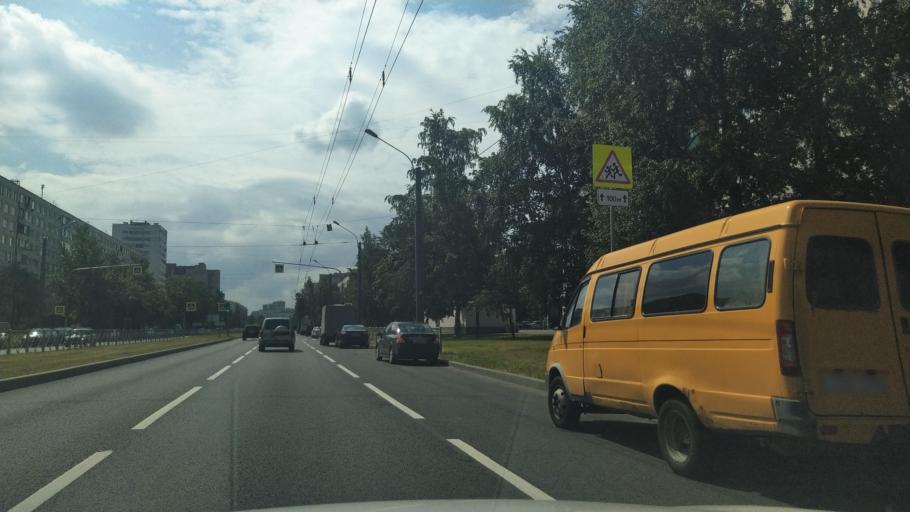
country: RU
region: Leningrad
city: Parnas
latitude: 60.0458
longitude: 30.3514
